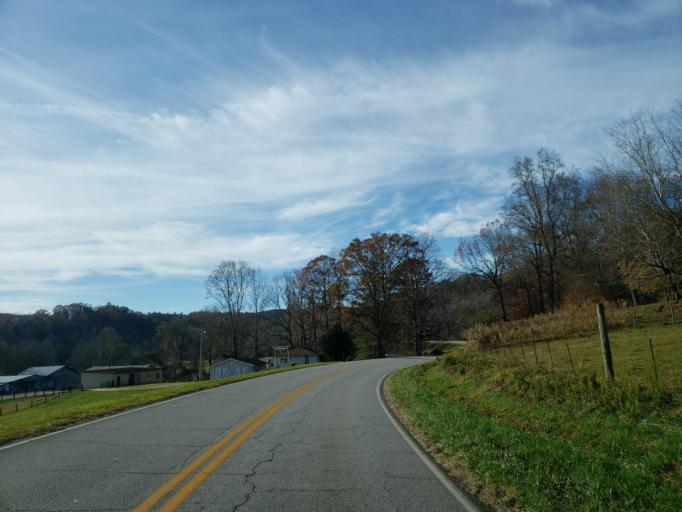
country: US
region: Georgia
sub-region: Lumpkin County
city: Dahlonega
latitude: 34.5868
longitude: -84.0292
